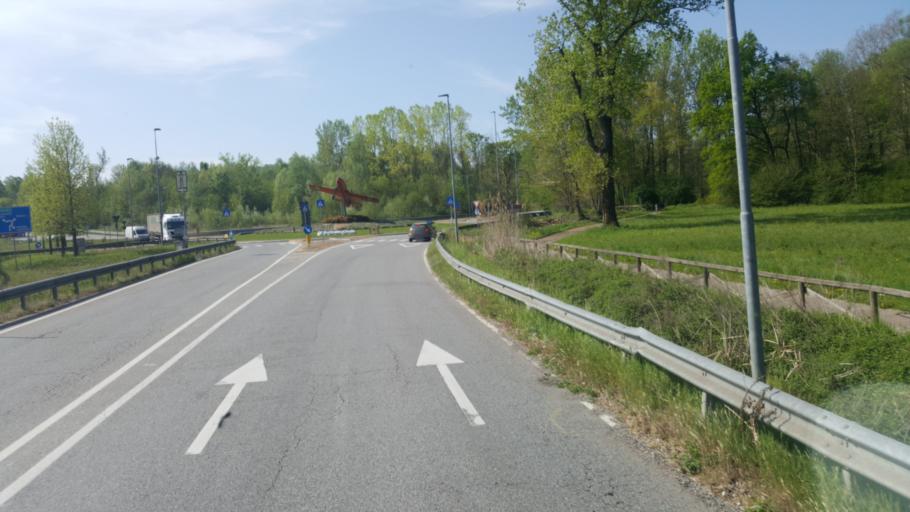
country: IT
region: Lombardy
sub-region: Provincia di Varese
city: Buguggiate
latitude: 45.7938
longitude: 8.8006
